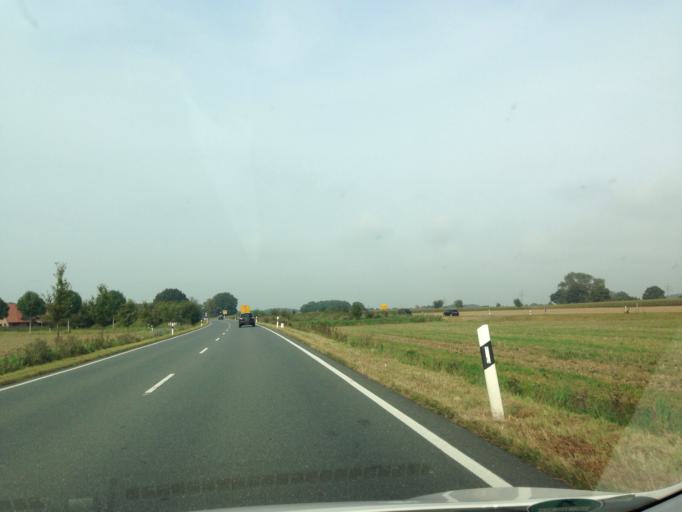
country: DE
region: North Rhine-Westphalia
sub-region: Regierungsbezirk Munster
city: Dulmen
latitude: 51.8246
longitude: 7.3314
